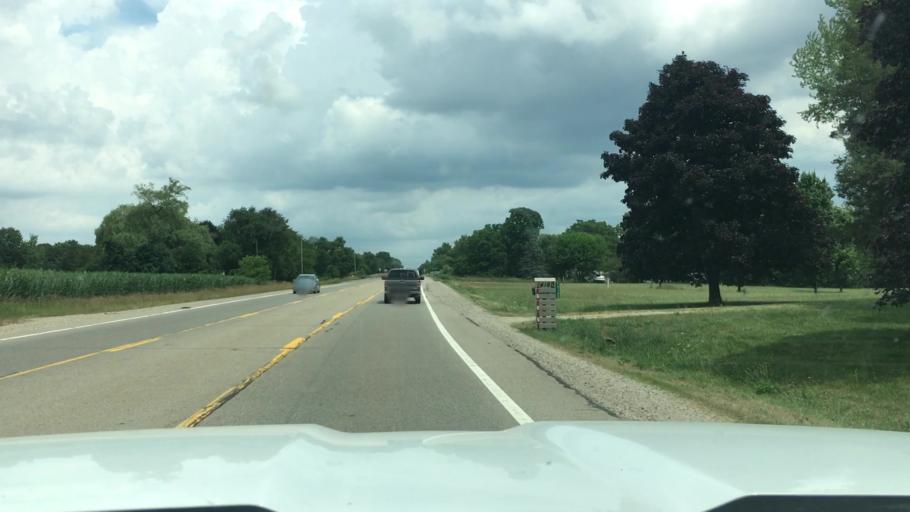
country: US
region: Michigan
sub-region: Montcalm County
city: Greenville
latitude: 43.1766
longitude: -85.3190
